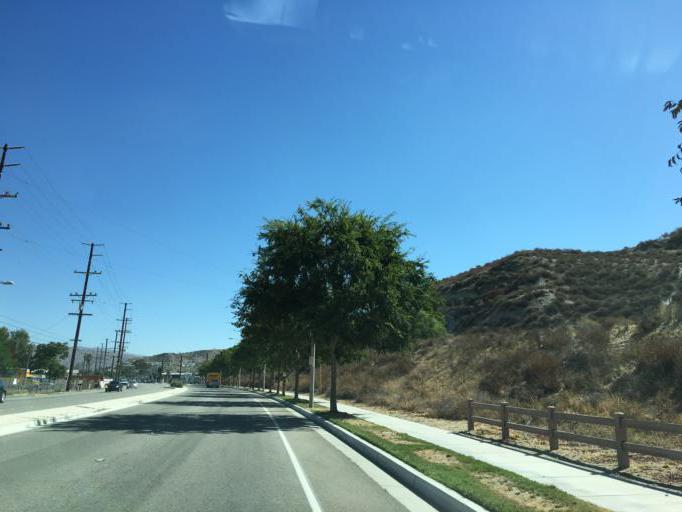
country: US
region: California
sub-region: Los Angeles County
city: Santa Clarita
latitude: 34.4357
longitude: -118.4337
